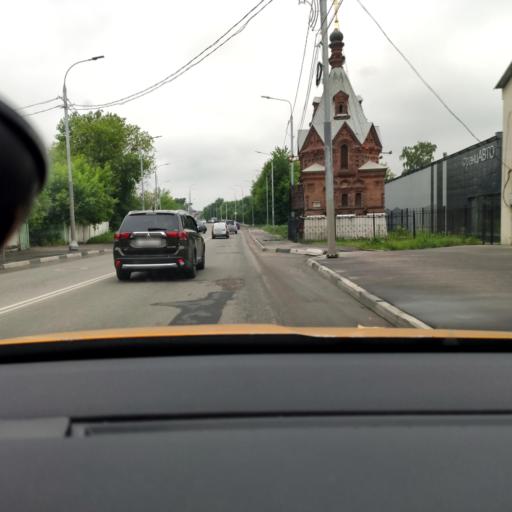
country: RU
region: Moskovskaya
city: Serpukhov
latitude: 54.9126
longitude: 37.4102
